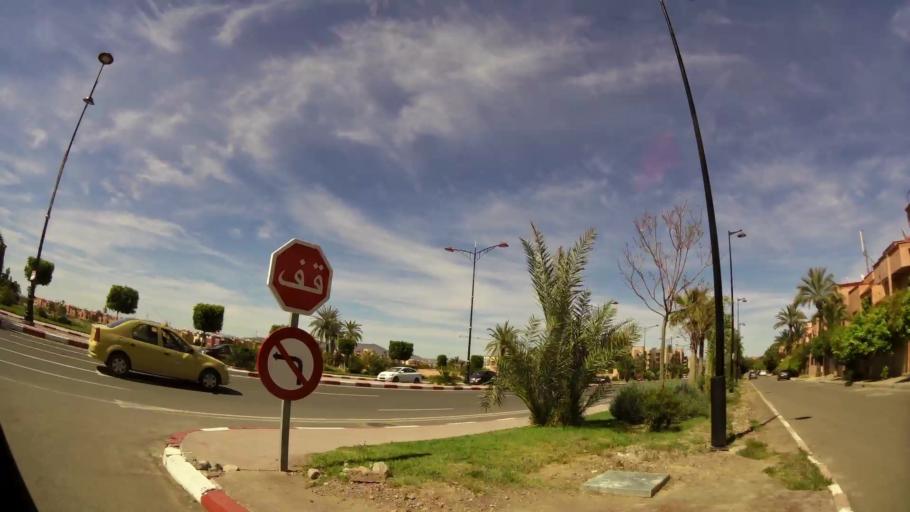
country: MA
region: Marrakech-Tensift-Al Haouz
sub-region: Marrakech
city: Marrakesh
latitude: 31.6743
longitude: -8.0039
